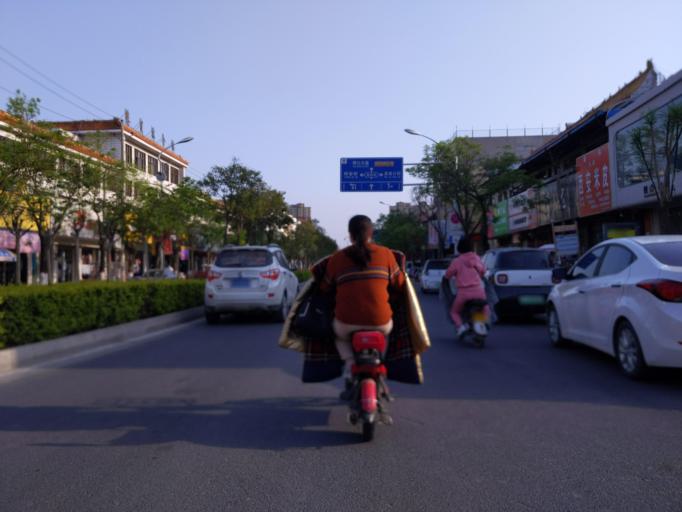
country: CN
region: Henan Sheng
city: Puyang Chengguanzhen
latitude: 35.7023
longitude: 115.0163
